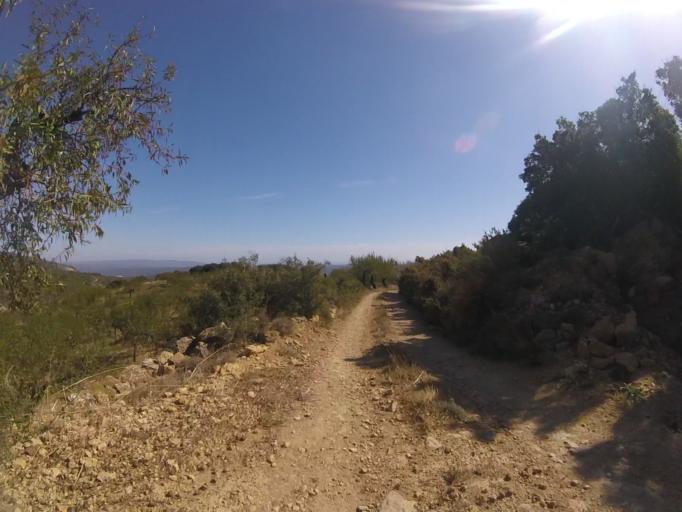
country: ES
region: Valencia
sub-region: Provincia de Castello
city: Sierra-Engarceran
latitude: 40.2720
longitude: 0.0062
